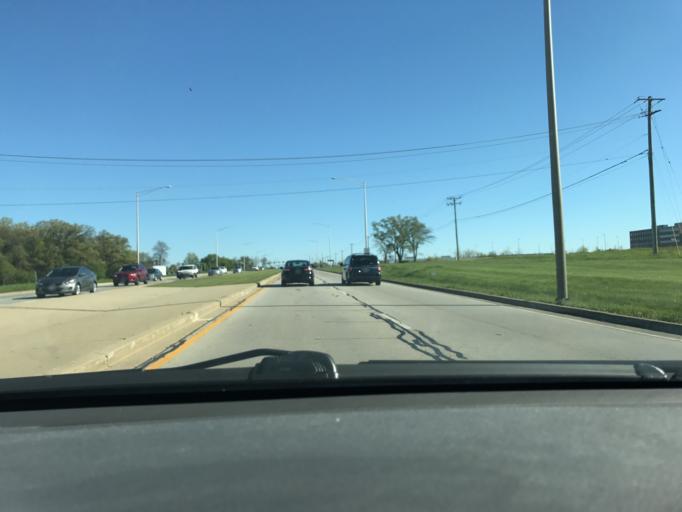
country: US
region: Illinois
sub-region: Kane County
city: Sleepy Hollow
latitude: 42.0665
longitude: -88.3356
